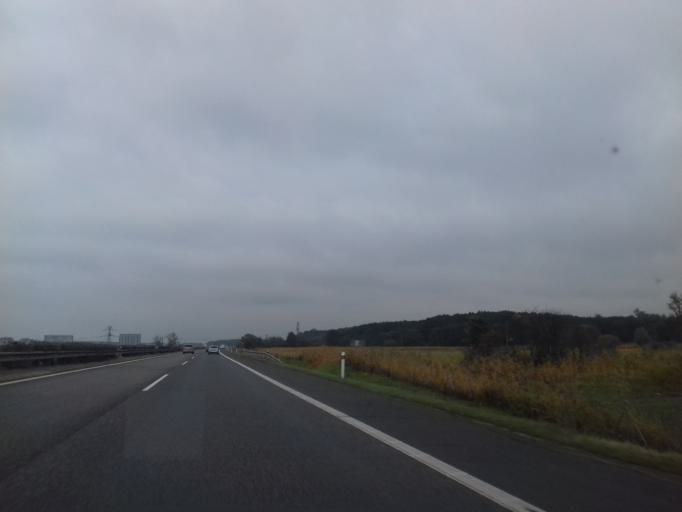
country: SK
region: Bratislavsky
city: Stupava
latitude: 48.3039
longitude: 17.0155
